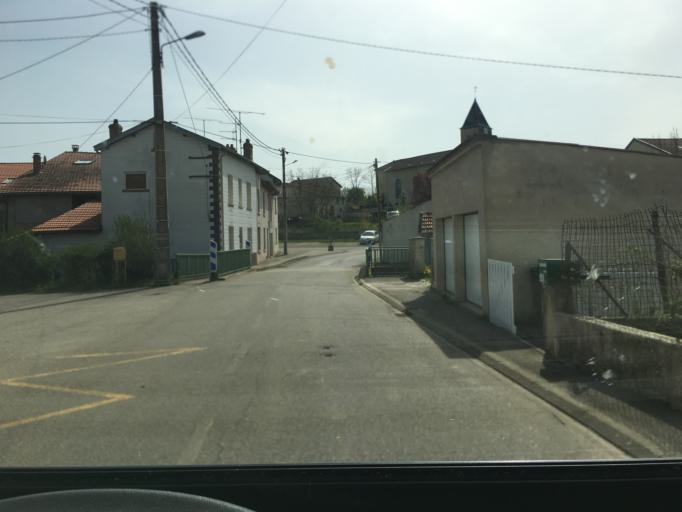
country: FR
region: Lorraine
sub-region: Departement de Meurthe-et-Moselle
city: Fleville-devant-Nancy
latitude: 48.6119
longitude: 6.2352
